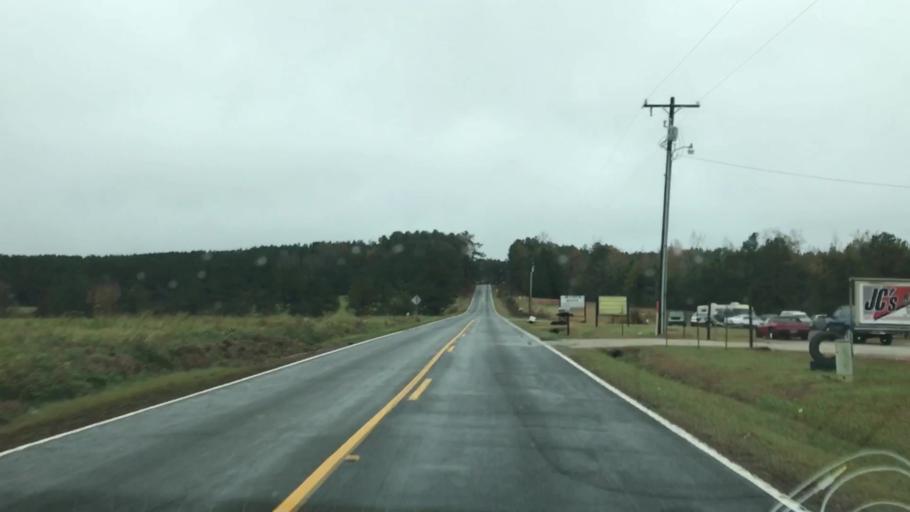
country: US
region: South Carolina
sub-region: Greenwood County
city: Ninety Six
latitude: 34.2989
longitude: -81.9765
